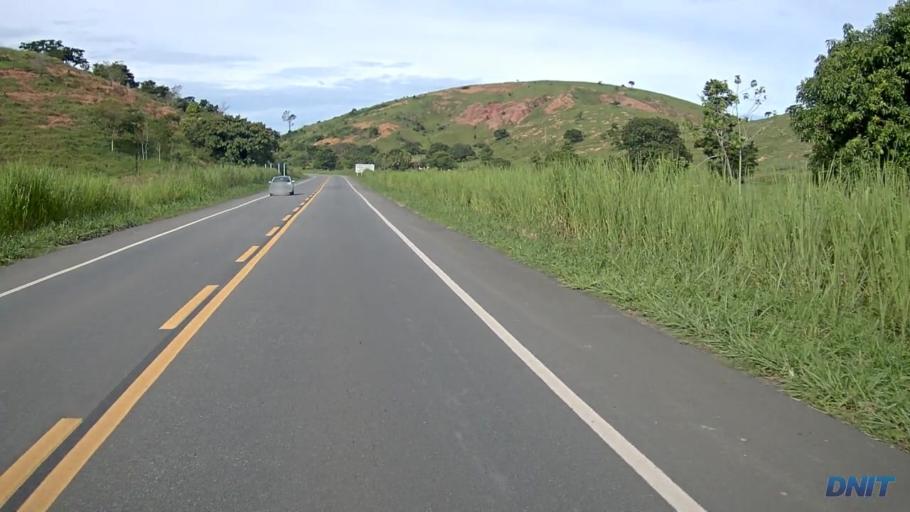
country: BR
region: Minas Gerais
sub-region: Belo Oriente
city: Belo Oriente
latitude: -19.2033
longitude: -42.2922
